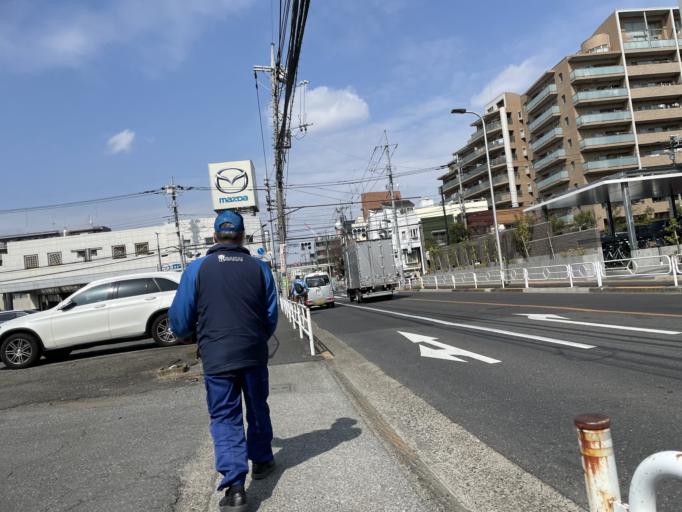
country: JP
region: Tokyo
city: Mitaka-shi
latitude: 35.6870
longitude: 139.5639
